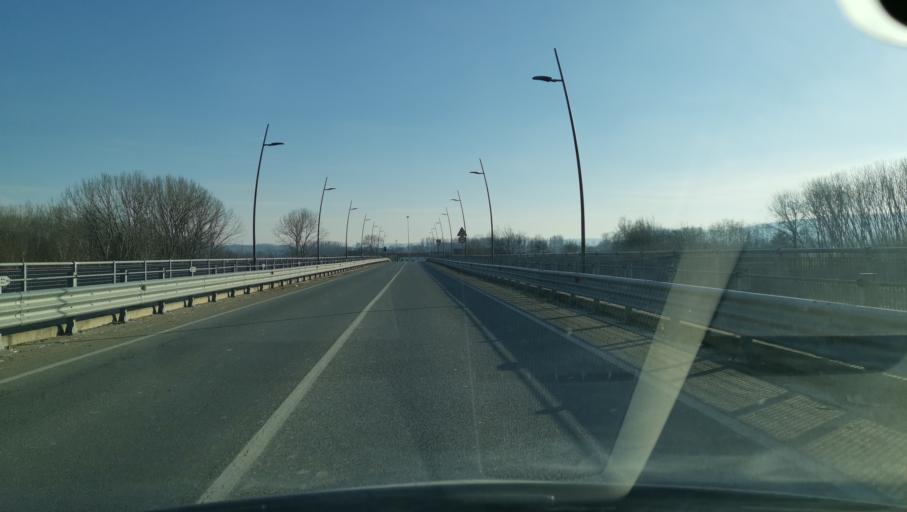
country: IT
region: Piedmont
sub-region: Provincia di Torino
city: Pavone Canavese
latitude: 45.4228
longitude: 7.8590
